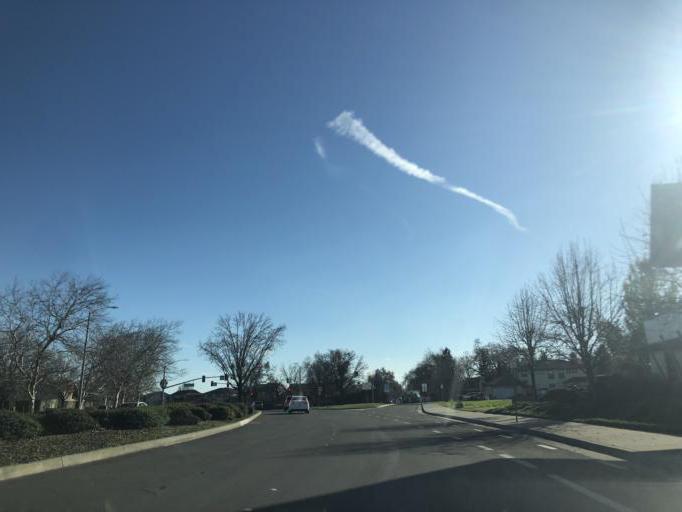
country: US
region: California
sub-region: Yolo County
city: Woodland
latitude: 38.6756
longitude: -121.7470
